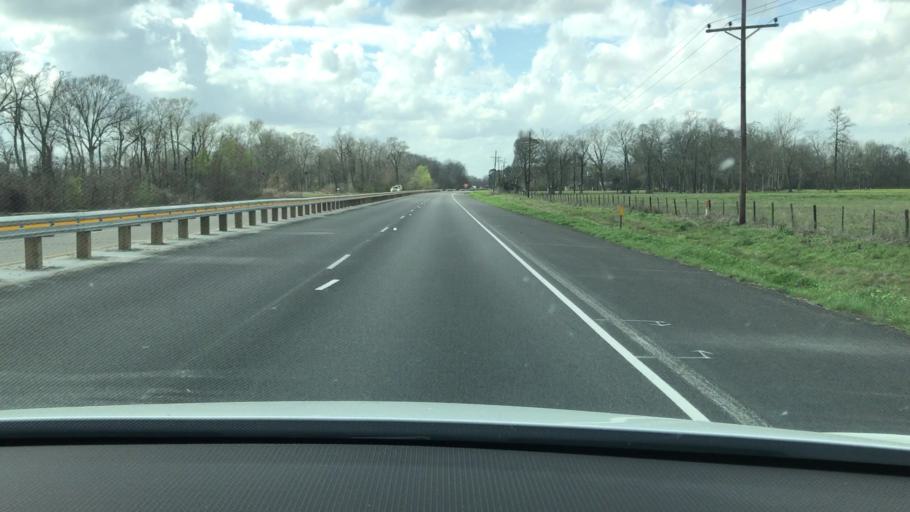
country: US
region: Louisiana
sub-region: Pointe Coupee Parish
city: Livonia
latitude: 30.5564
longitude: -91.6273
